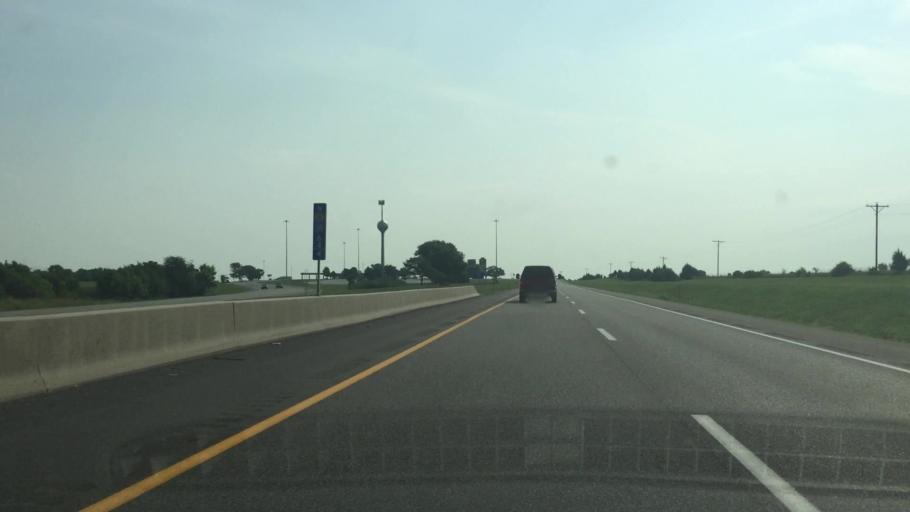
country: US
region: Kansas
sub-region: Butler County
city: Towanda
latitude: 37.7631
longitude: -96.9900
